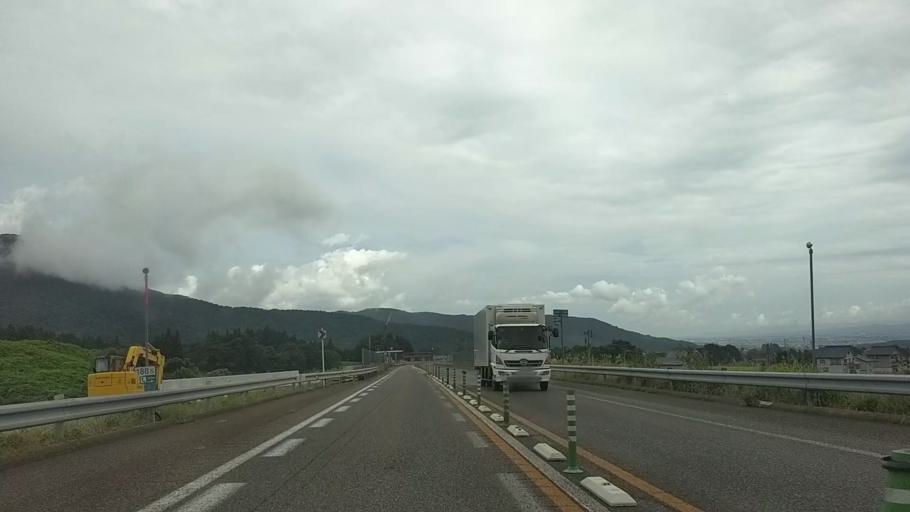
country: JP
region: Niigata
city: Arai
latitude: 37.0017
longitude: 138.2077
